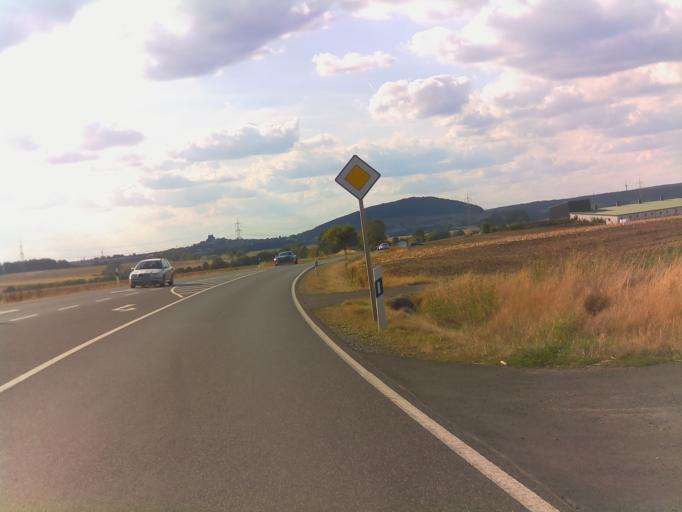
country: DE
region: Hesse
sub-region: Regierungsbezirk Kassel
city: Dipperz
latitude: 50.5451
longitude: 9.7743
